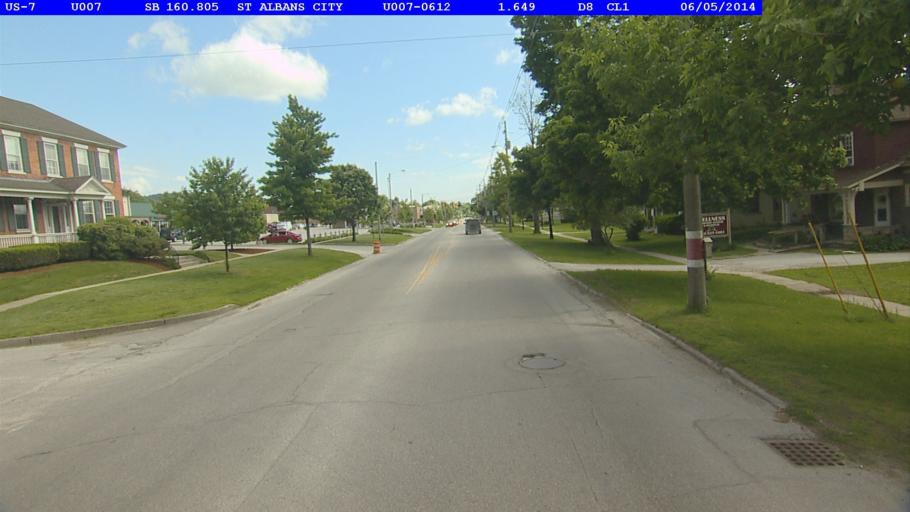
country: US
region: Vermont
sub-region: Franklin County
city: Saint Albans
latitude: 44.8165
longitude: -73.0824
